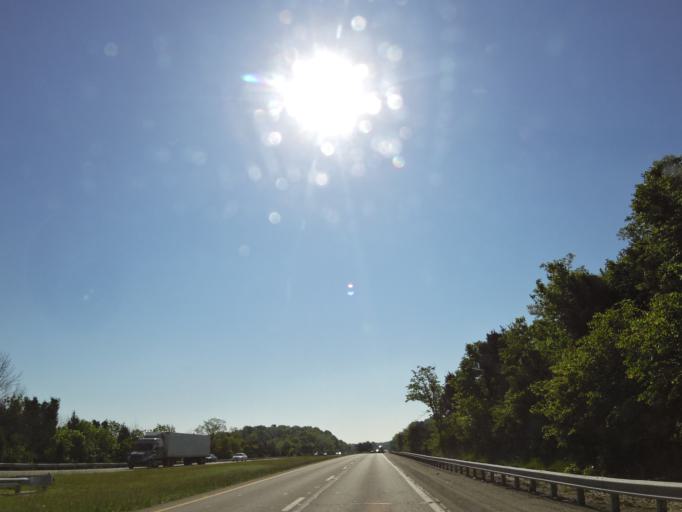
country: US
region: Kentucky
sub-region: Franklin County
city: Frankfort
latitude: 38.1467
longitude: -85.0153
